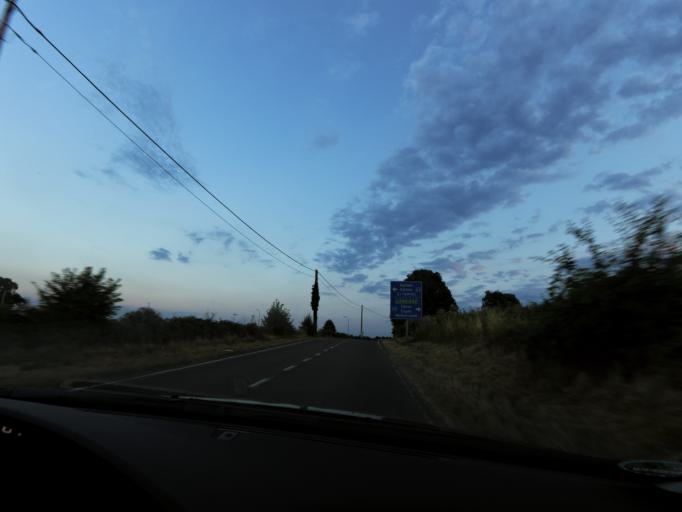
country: BE
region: Wallonia
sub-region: Province de Liege
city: La Calamine
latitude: 50.7043
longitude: 5.9826
